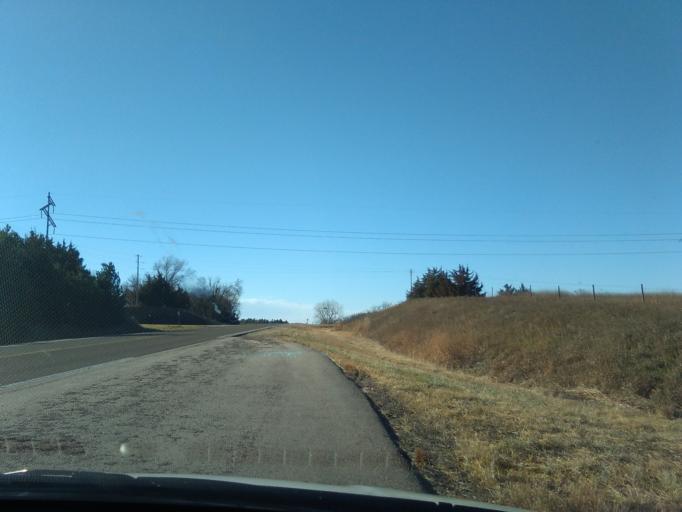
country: US
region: Nebraska
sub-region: Adams County
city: Hastings
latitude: 40.4373
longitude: -98.3715
